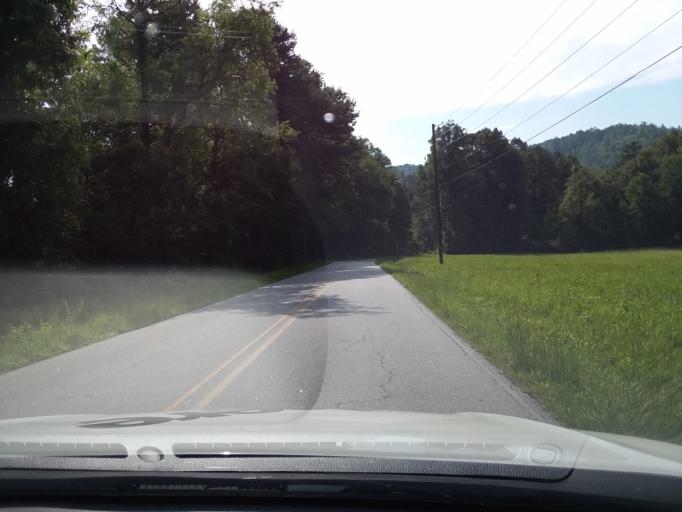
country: US
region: Georgia
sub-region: Rabun County
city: Clayton
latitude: 34.7765
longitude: -83.3984
